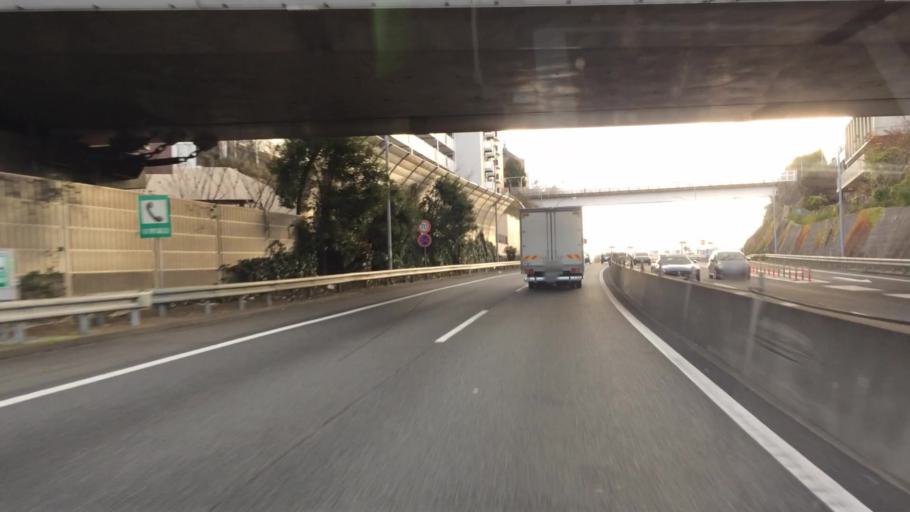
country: JP
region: Kanagawa
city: Yokohama
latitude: 35.4340
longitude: 139.5541
